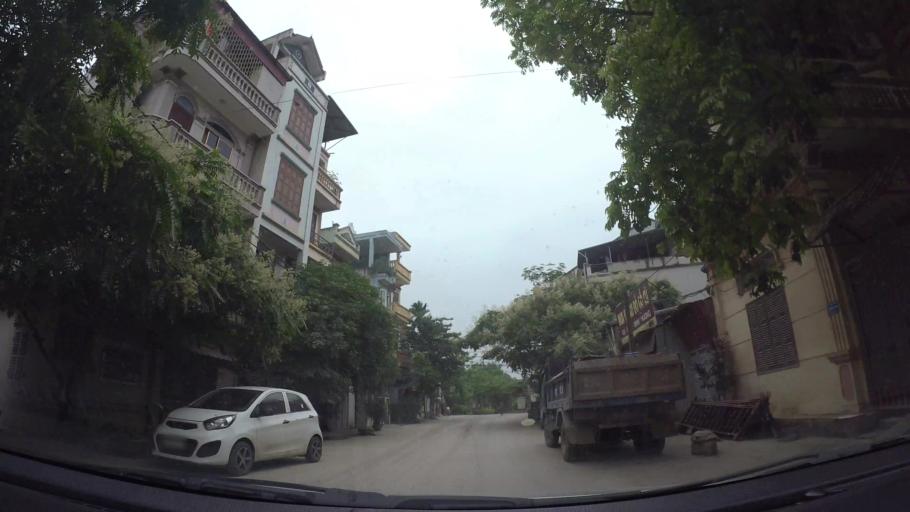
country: VN
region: Ha Noi
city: Tay Ho
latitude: 21.0816
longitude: 105.8201
